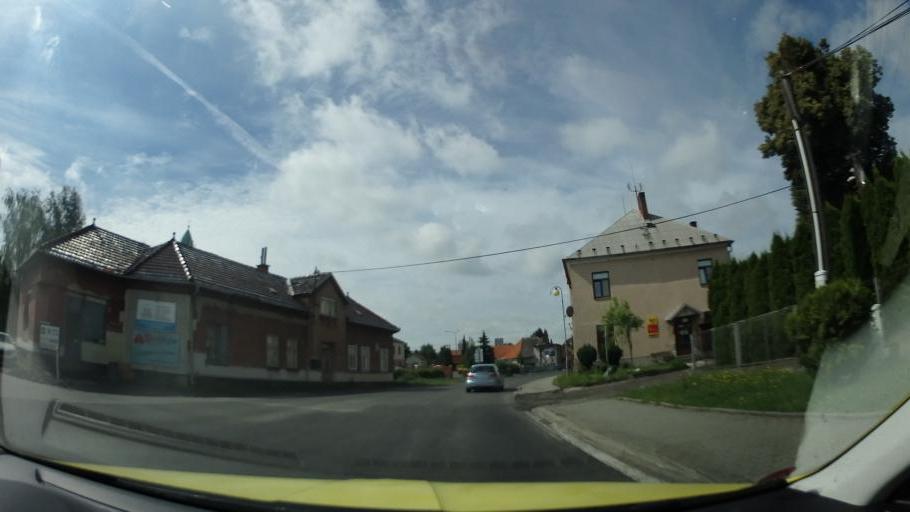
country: CZ
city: Hodslavice
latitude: 49.5390
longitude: 18.0238
